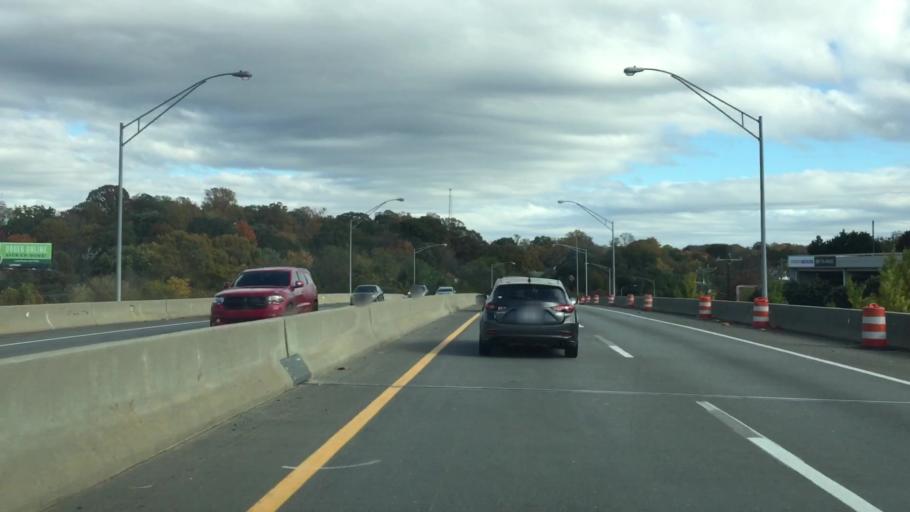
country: US
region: North Carolina
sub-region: Forsyth County
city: Winston-Salem
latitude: 36.0918
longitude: -80.2664
